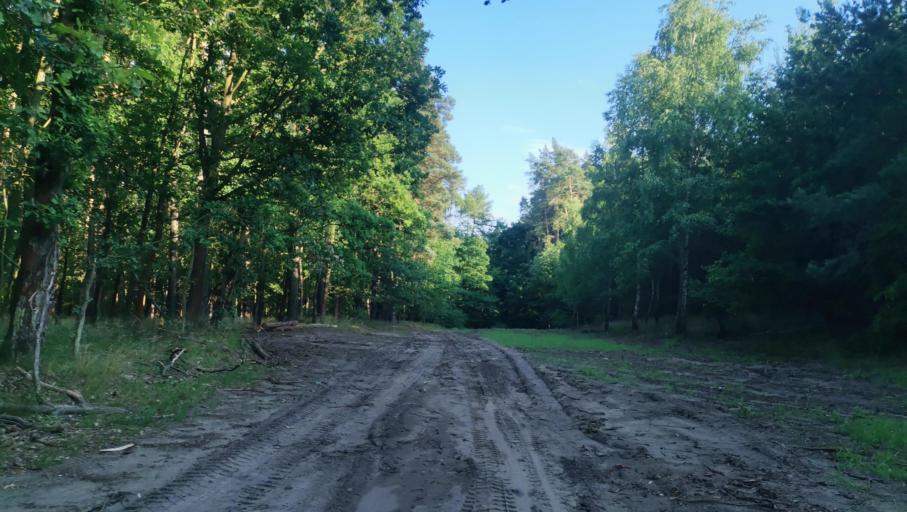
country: PL
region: Greater Poland Voivodeship
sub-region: Powiat jarocinski
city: Jarocin
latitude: 51.9825
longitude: 17.5442
